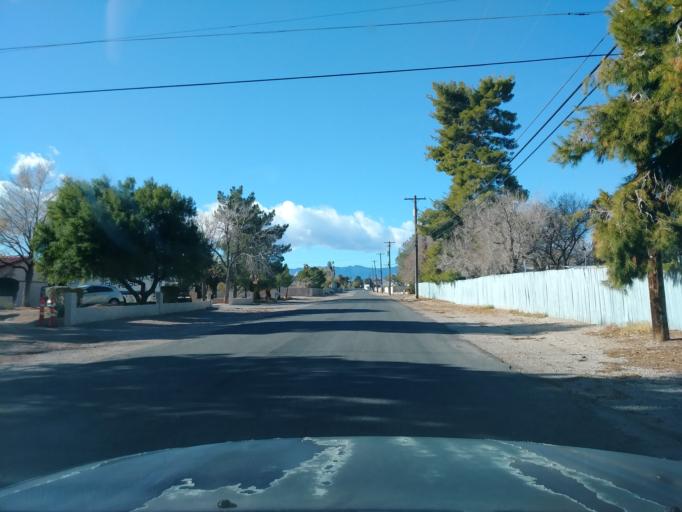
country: US
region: Nevada
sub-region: Clark County
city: Spring Valley
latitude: 36.1499
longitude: -115.2199
